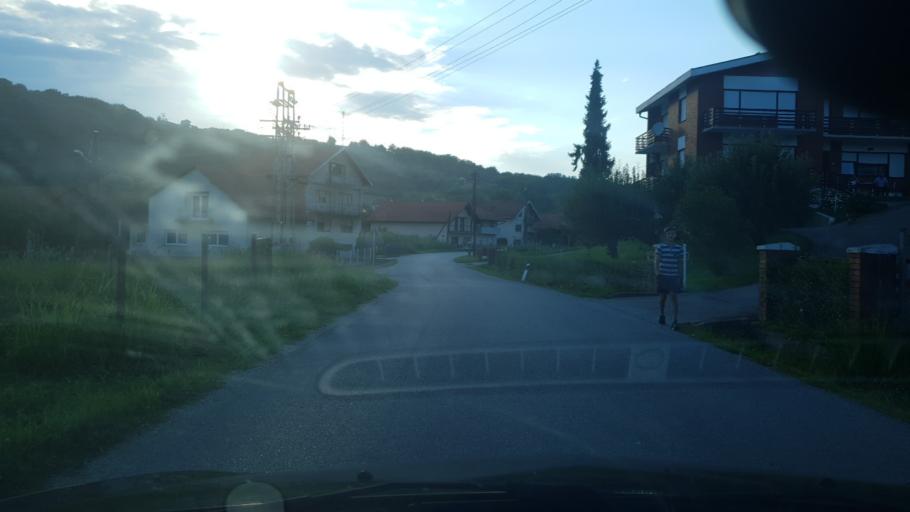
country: HR
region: Krapinsko-Zagorska
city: Zabok
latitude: 46.0390
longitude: 15.8919
